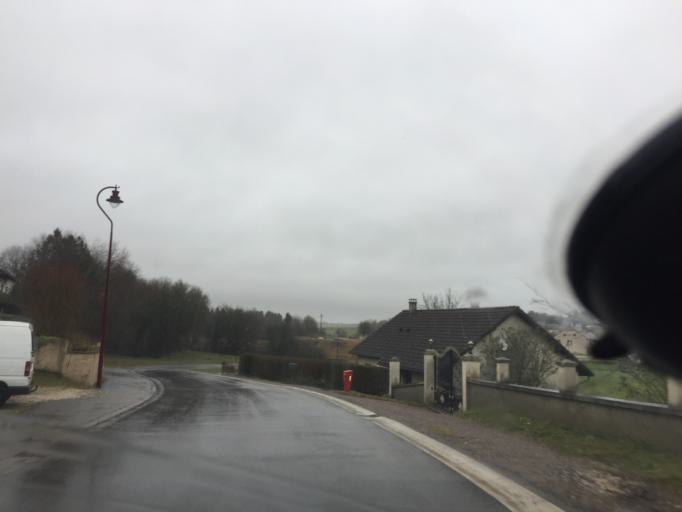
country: FR
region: Franche-Comte
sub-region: Departement du Jura
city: Orchamps
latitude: 47.1512
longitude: 5.6065
